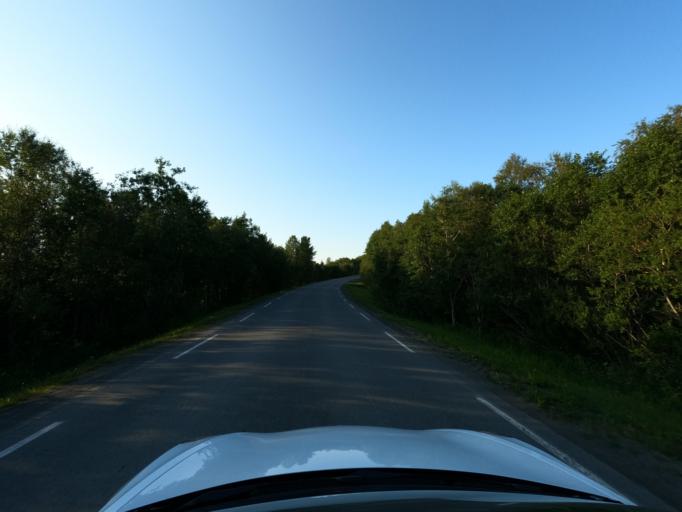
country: NO
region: Troms
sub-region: Skanland
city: Evenskjer
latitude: 68.4854
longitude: 16.7118
